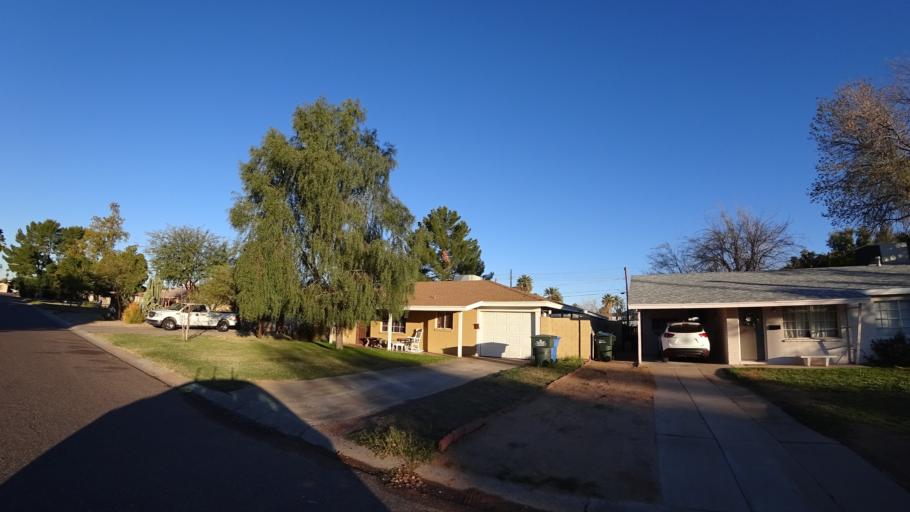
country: US
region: Arizona
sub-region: Maricopa County
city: Paradise Valley
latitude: 33.4868
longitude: -111.9983
